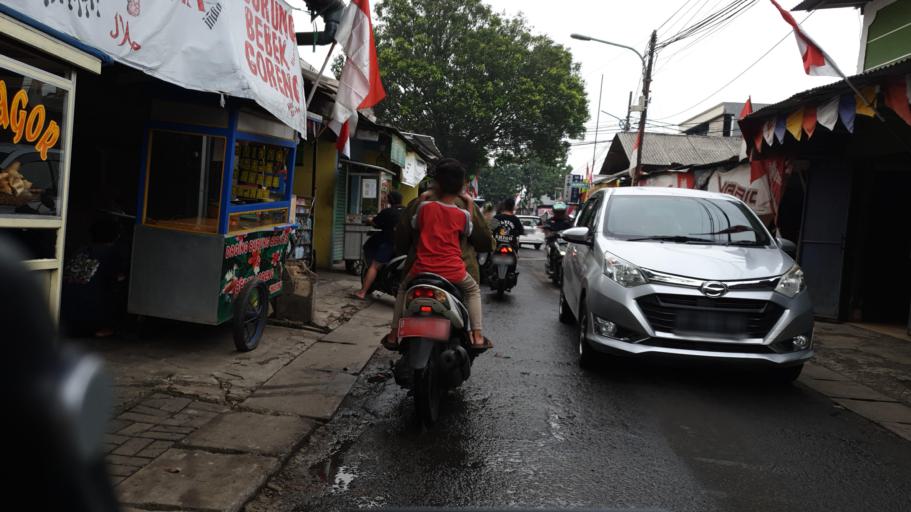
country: ID
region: West Java
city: Pamulang
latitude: -6.3309
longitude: 106.7698
